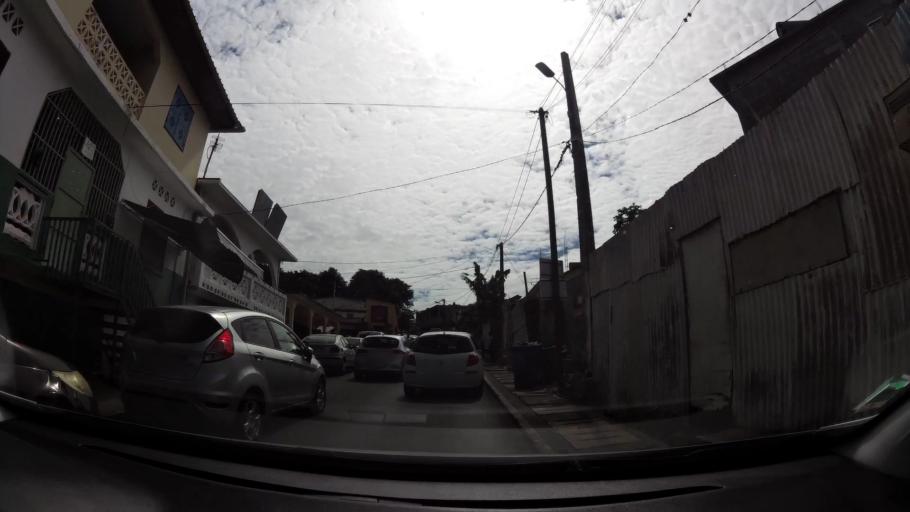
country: YT
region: Mamoudzou
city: Mamoudzou
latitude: -12.7810
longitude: 45.2296
